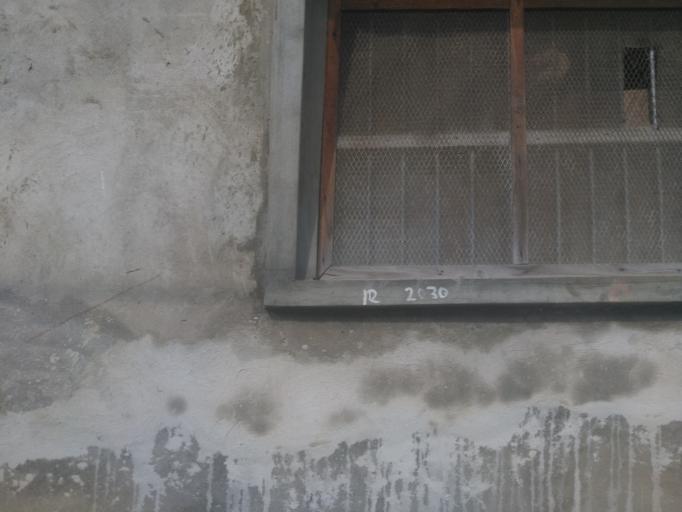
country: TZ
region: Zanzibar Urban/West
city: Zanzibar
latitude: -6.1604
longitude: 39.2057
